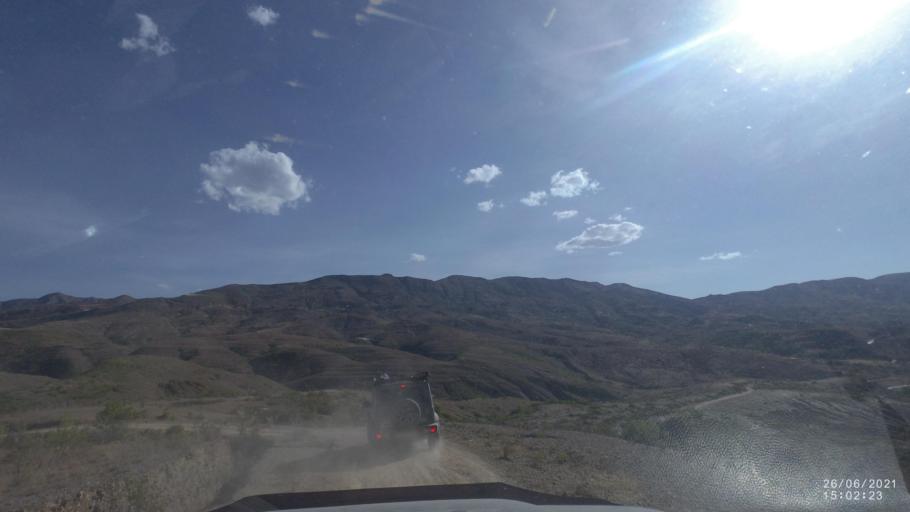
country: BO
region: Cochabamba
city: Mizque
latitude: -17.9498
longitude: -65.6268
